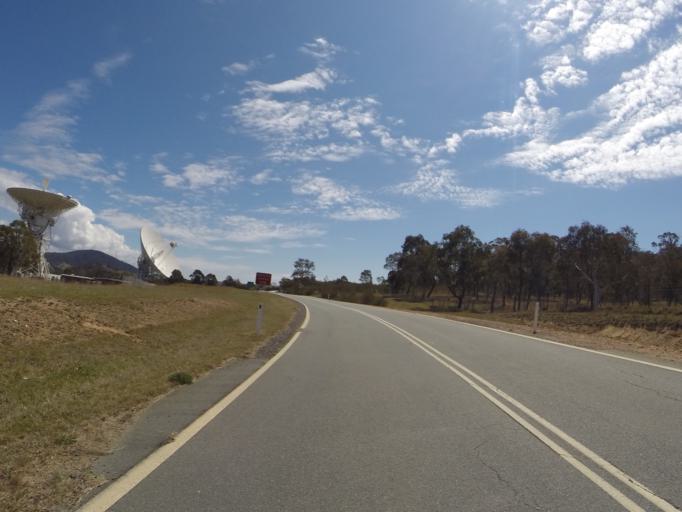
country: AU
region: Australian Capital Territory
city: Macarthur
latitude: -35.4062
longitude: 148.9844
